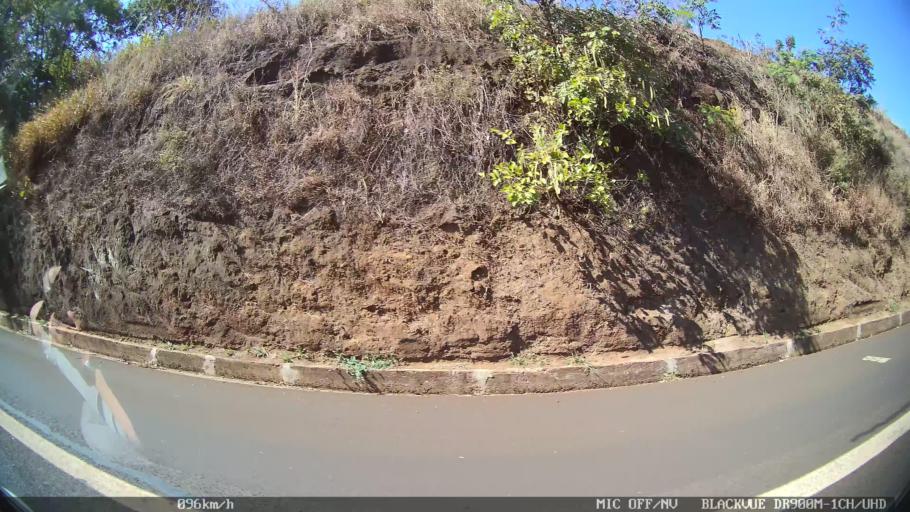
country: BR
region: Sao Paulo
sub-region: Batatais
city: Batatais
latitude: -20.7373
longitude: -47.5301
